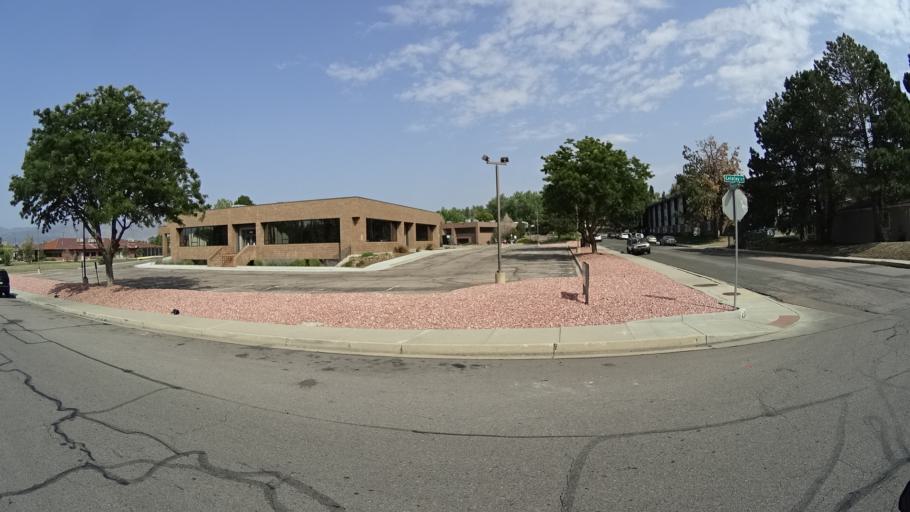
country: US
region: Colorado
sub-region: El Paso County
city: Colorado Springs
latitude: 38.8569
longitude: -104.7891
